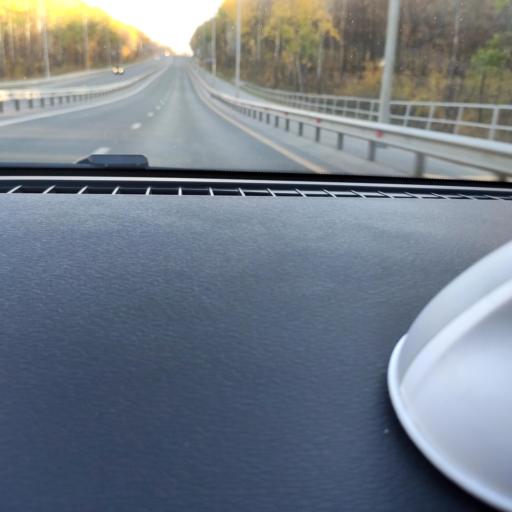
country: RU
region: Samara
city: Petra-Dubrava
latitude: 53.2895
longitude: 50.2485
